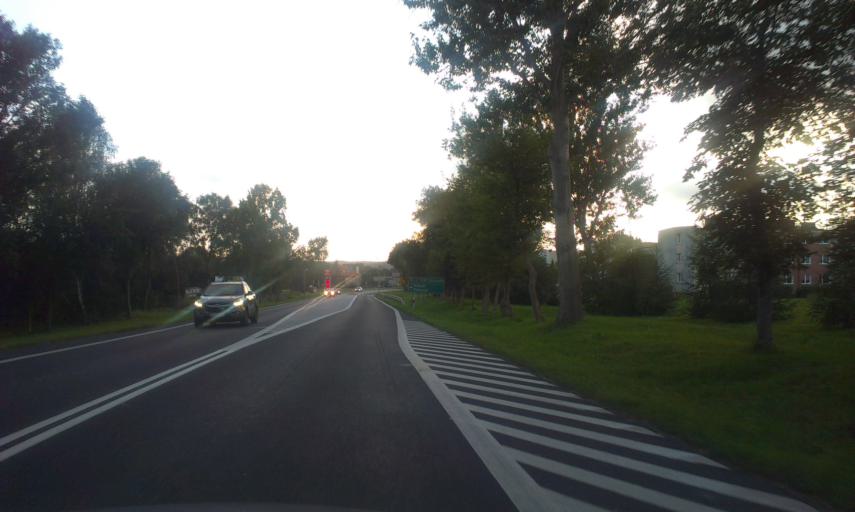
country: PL
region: West Pomeranian Voivodeship
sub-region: Powiat koszalinski
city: Sianow
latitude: 54.2322
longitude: 16.3105
